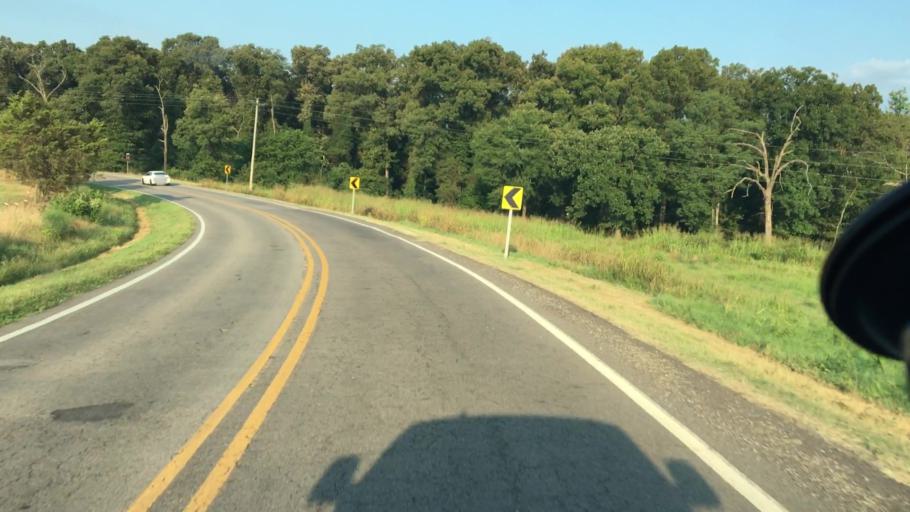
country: US
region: Arkansas
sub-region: Johnson County
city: Coal Hill
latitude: 35.3793
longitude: -93.5602
